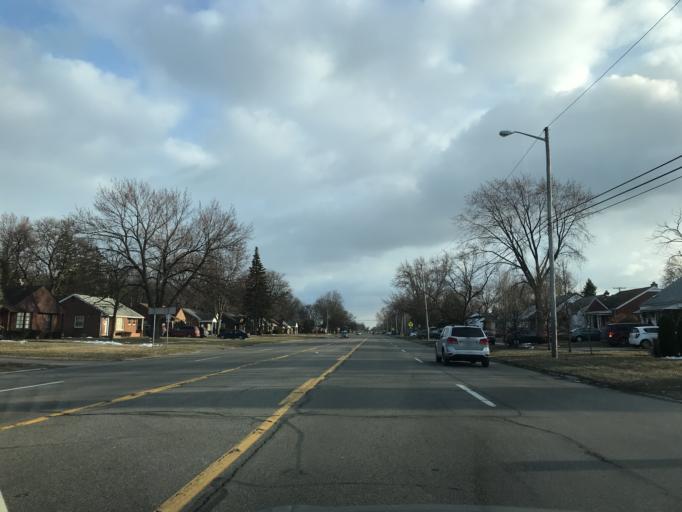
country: US
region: Michigan
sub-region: Wayne County
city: Redford
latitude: 42.4414
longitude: -83.2975
